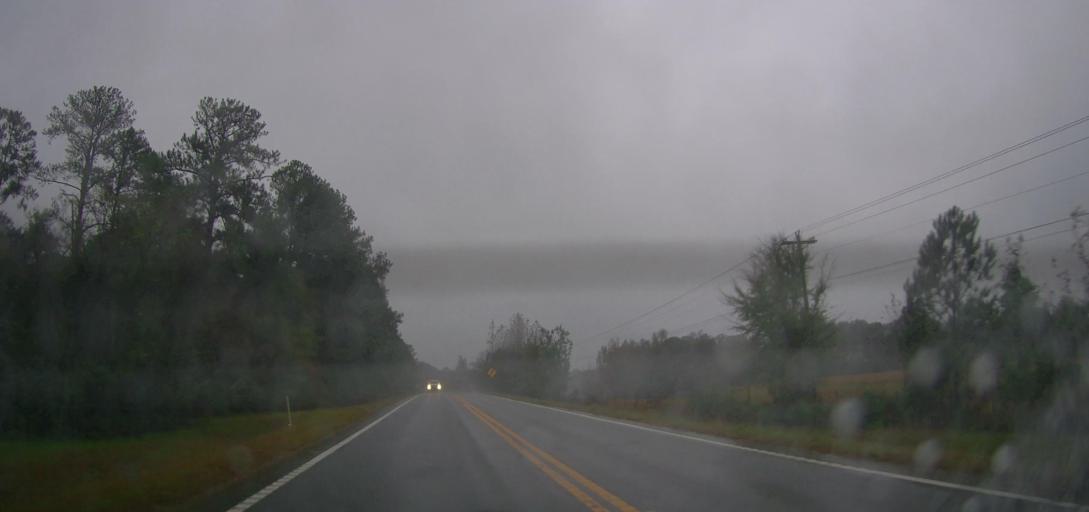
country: US
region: Georgia
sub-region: Jones County
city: Gray
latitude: 33.0349
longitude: -83.5165
